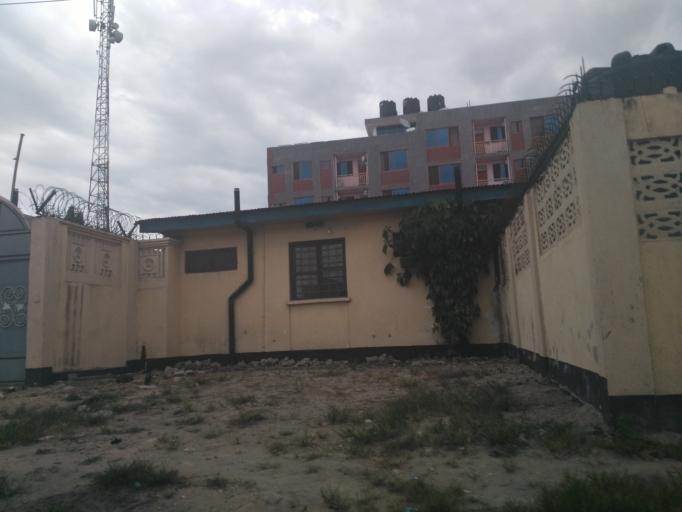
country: TZ
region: Dar es Salaam
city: Magomeni
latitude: -6.7920
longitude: 39.2675
